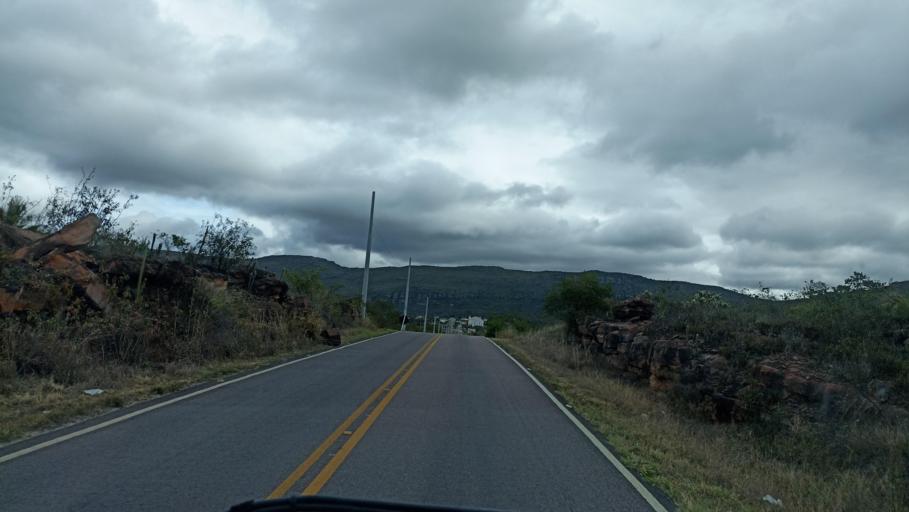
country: BR
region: Bahia
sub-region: Andarai
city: Vera Cruz
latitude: -12.9981
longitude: -41.3610
